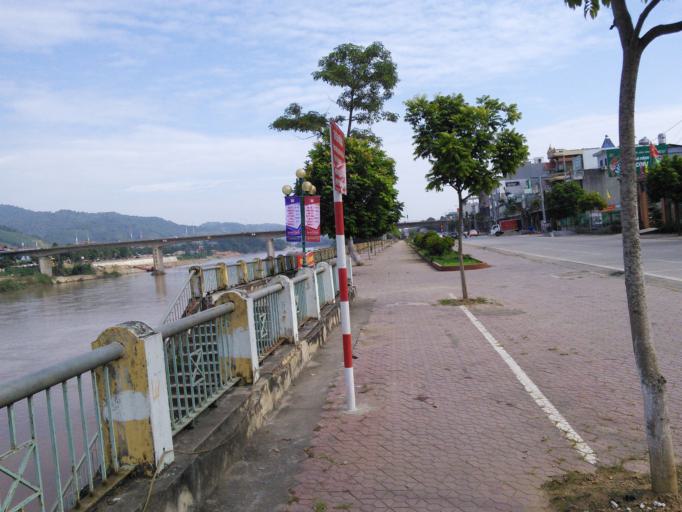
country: VN
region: Lao Cai
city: Lao Cai
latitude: 22.4862
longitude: 103.9755
